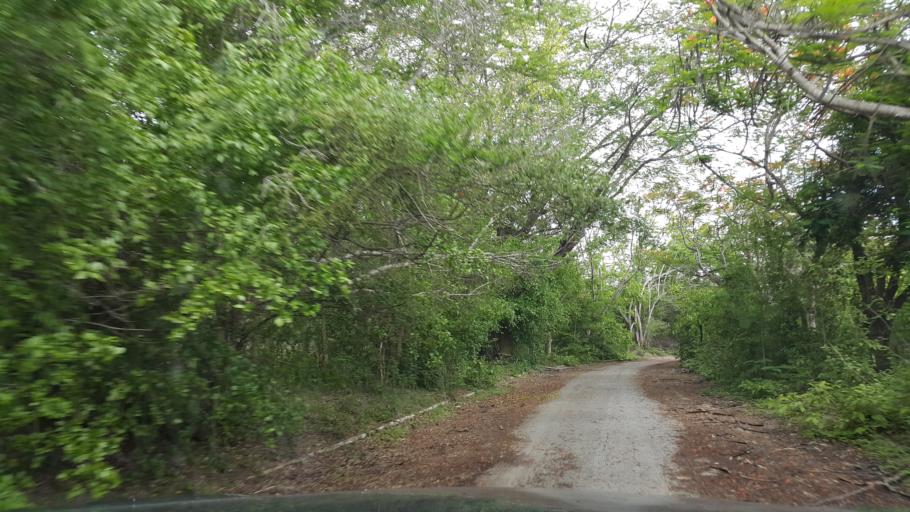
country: TH
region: Chiang Mai
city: San Kamphaeng
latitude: 18.7572
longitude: 99.1190
